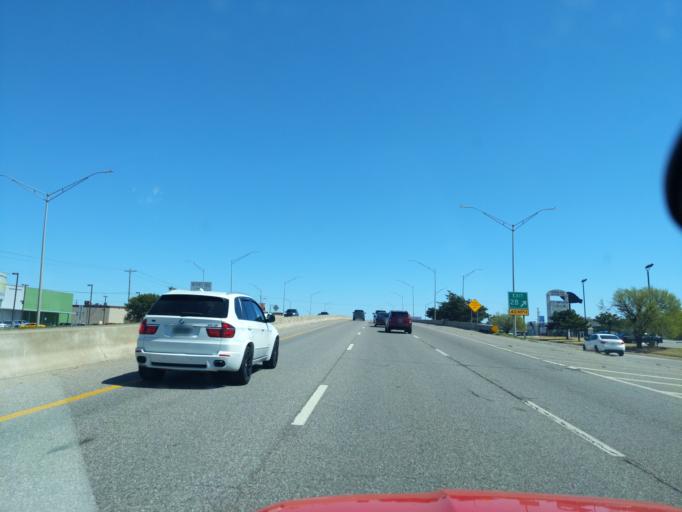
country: US
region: Oklahoma
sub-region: Cleveland County
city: Moore
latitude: 35.3914
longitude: -97.5239
